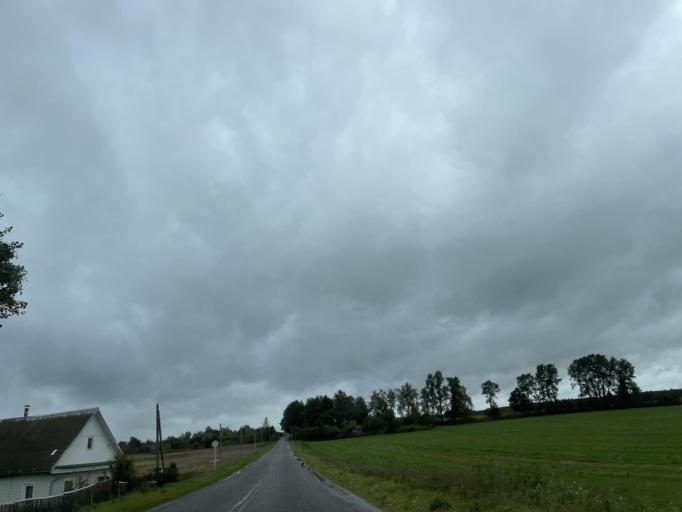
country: BY
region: Minsk
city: Snow
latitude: 53.2096
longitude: 26.2342
